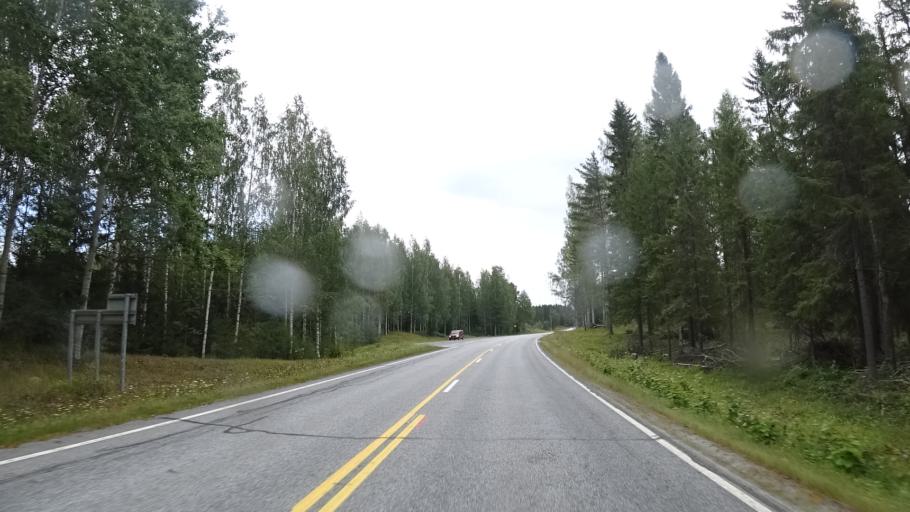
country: FI
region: North Karelia
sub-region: Keski-Karjala
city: Raeaekkylae
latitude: 62.1061
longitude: 29.6854
